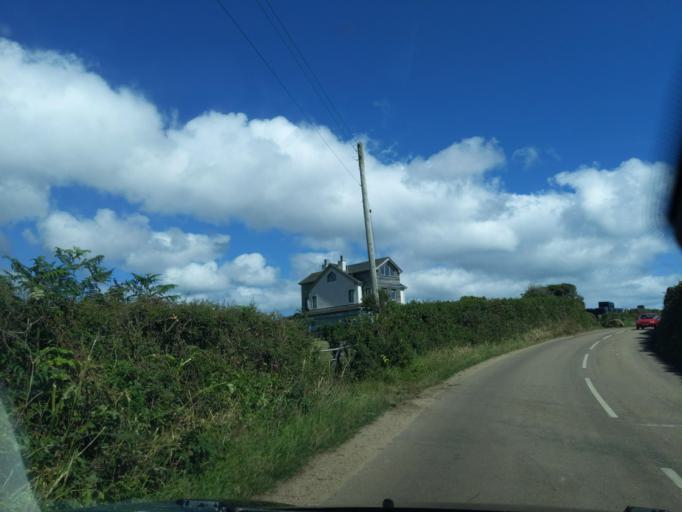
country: GB
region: England
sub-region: Cornwall
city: St. Buryan
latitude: 50.0548
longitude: -5.6543
